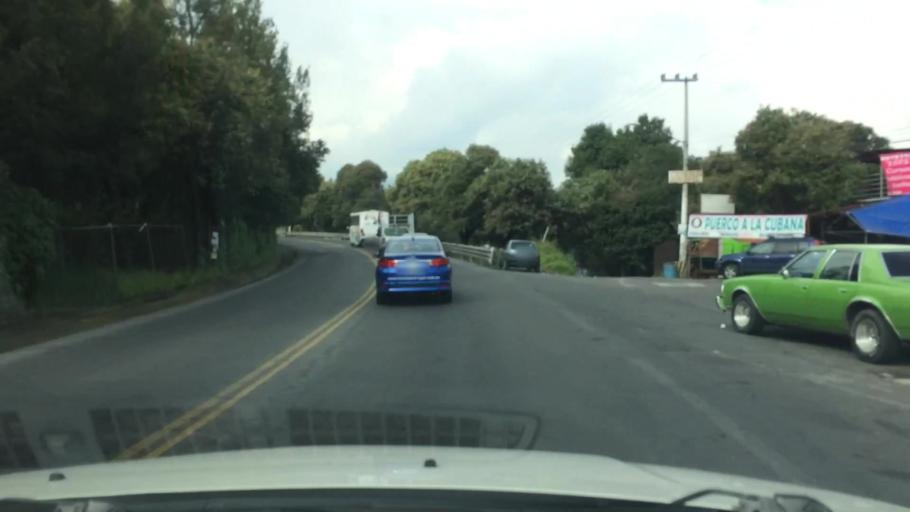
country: MX
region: Mexico City
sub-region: Tlalpan
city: Lomas de Tepemecatl
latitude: 19.2680
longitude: -99.2230
